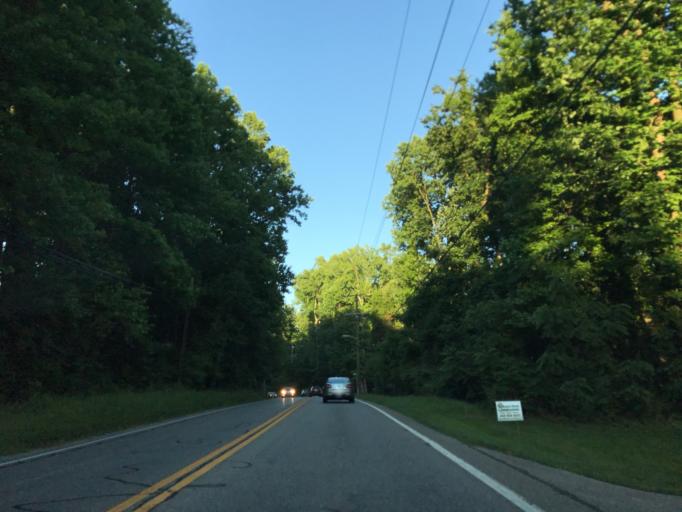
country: US
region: Maryland
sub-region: Anne Arundel County
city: Selby-on-the-Bay
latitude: 38.9060
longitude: -76.5309
